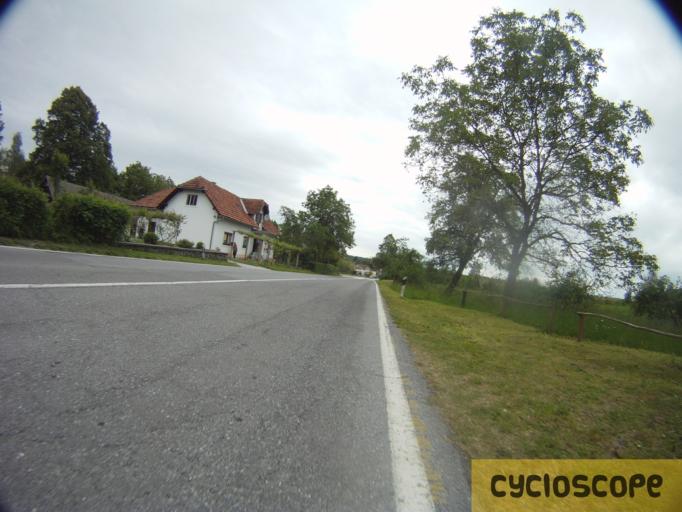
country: SI
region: Crnomelj
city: Crnomelj
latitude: 45.4403
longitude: 15.2597
